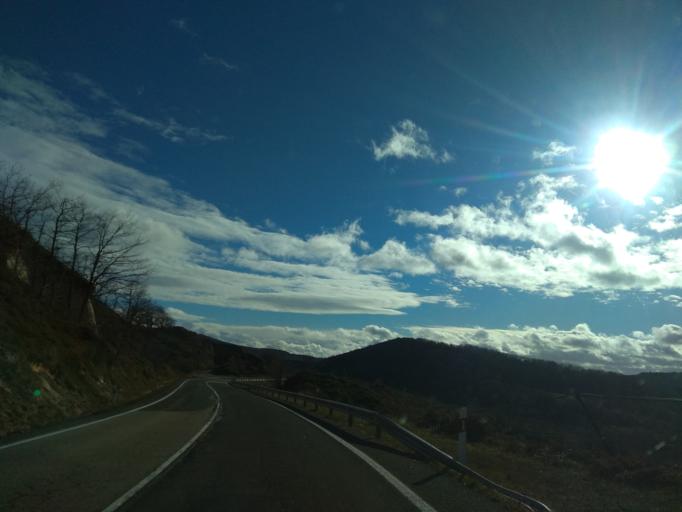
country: ES
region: Cantabria
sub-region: Provincia de Cantabria
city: San Martin de Elines
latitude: 42.9368
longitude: -3.8299
